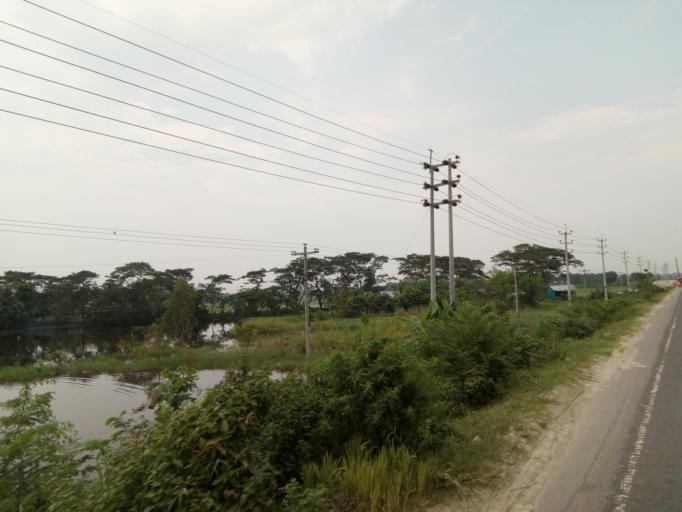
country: BD
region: Dhaka
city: Dohar
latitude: 23.5114
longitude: 90.2769
